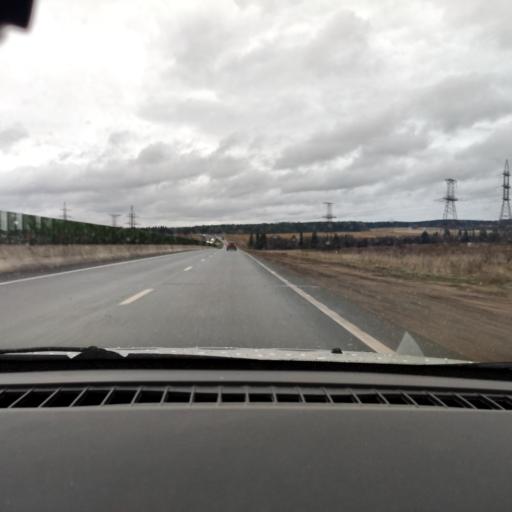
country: RU
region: Perm
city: Ferma
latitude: 57.9358
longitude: 56.3601
